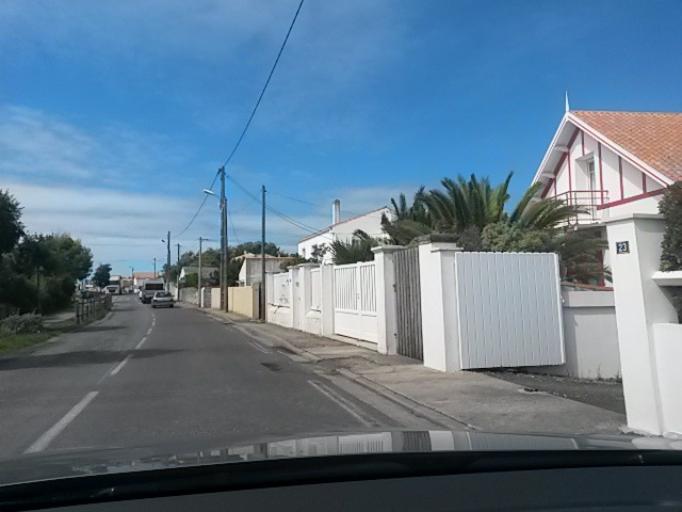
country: FR
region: Poitou-Charentes
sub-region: Departement de la Charente-Maritime
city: Dolus-d'Oleron
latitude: 45.9142
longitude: -1.3234
